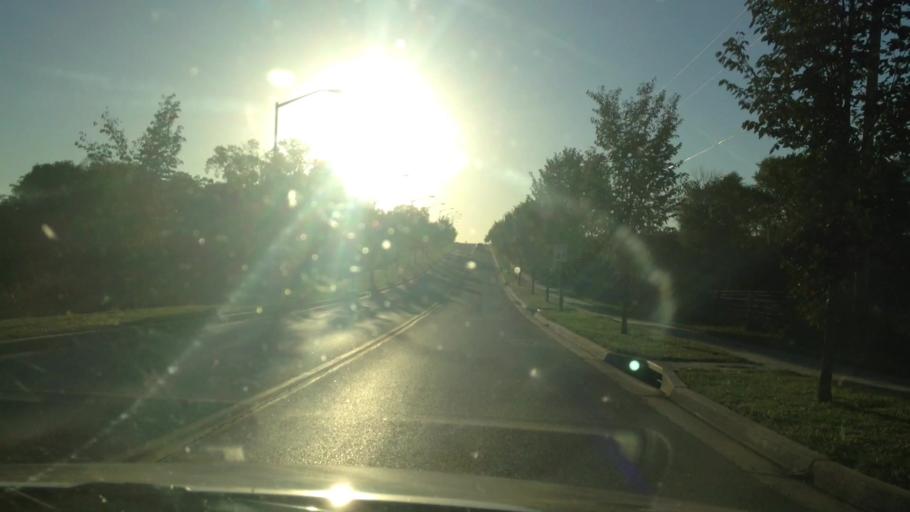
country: US
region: Missouri
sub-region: Clay County
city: Pleasant Valley
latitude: 39.2887
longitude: -94.5017
